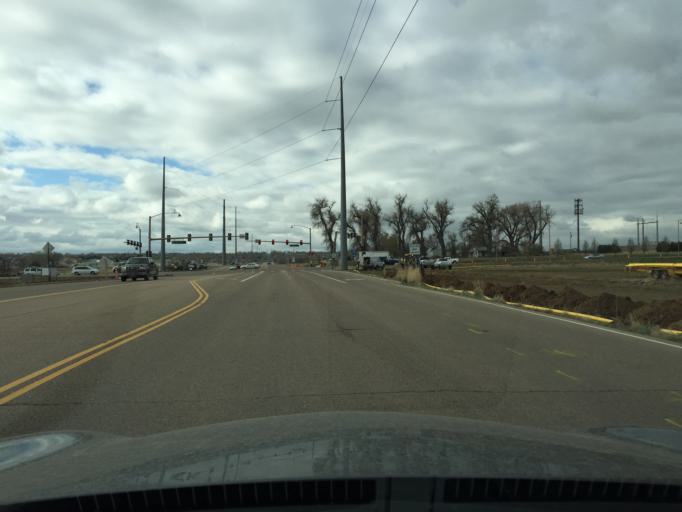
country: US
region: Colorado
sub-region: Adams County
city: Northglenn
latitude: 39.9588
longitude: -104.9784
